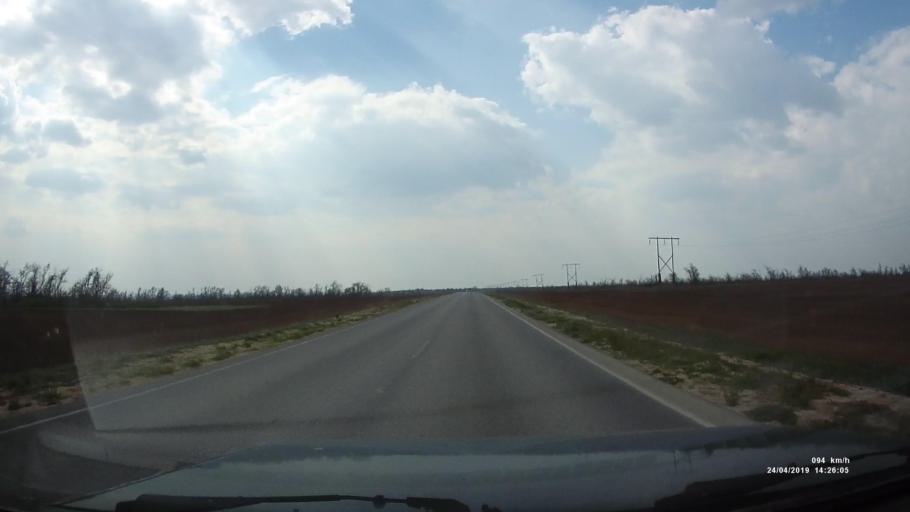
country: RU
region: Kalmykiya
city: Arshan'
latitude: 46.3326
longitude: 44.0696
